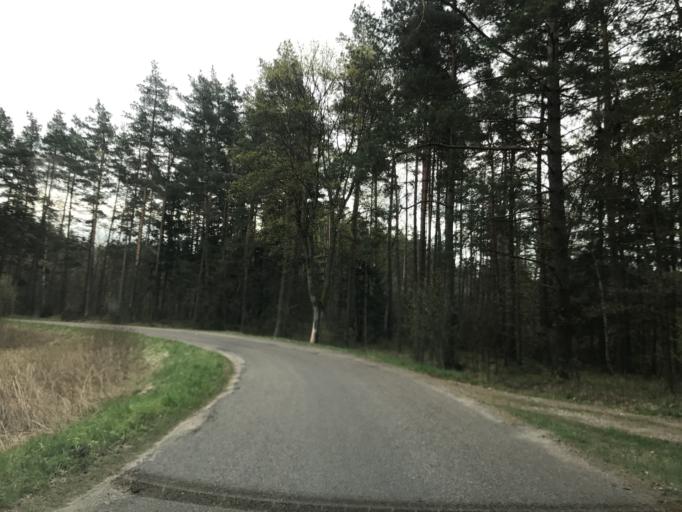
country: PL
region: Warmian-Masurian Voivodeship
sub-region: Powiat olsztynski
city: Olsztynek
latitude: 53.6141
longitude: 20.2405
